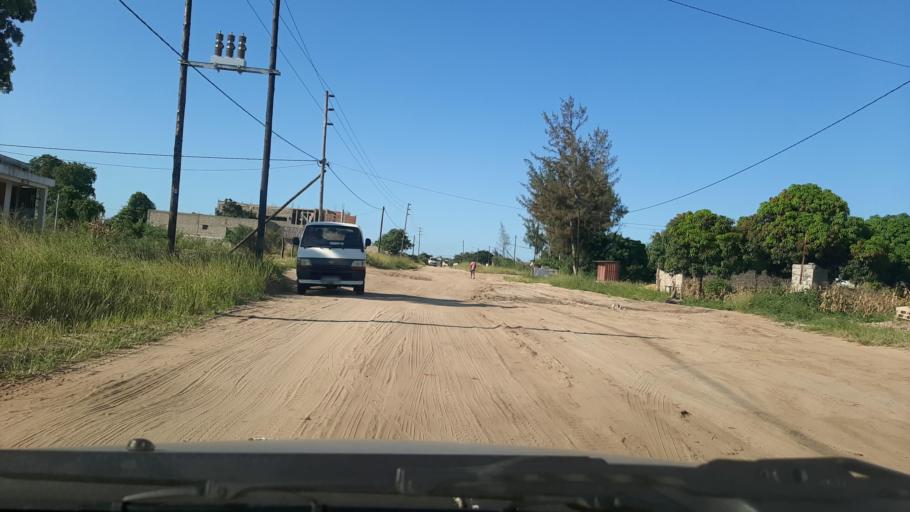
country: MZ
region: Maputo City
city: Maputo
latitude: -25.7607
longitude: 32.5489
